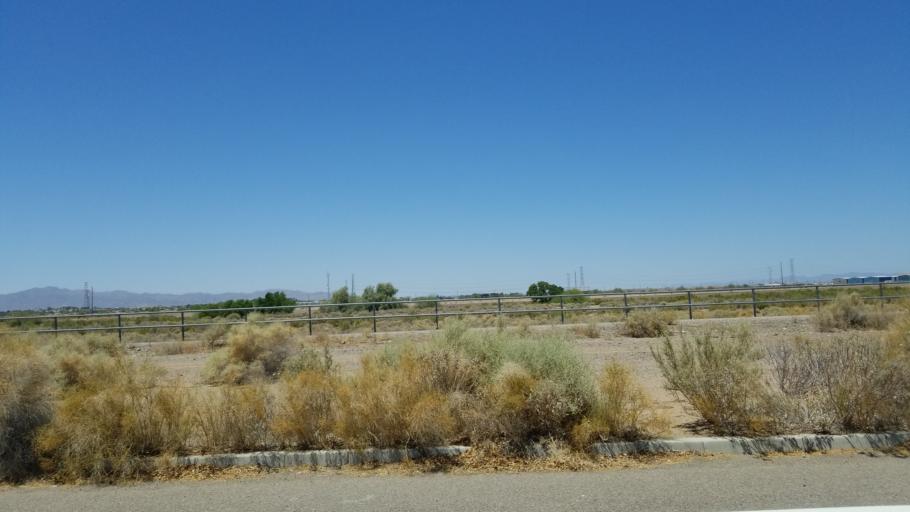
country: US
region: Arizona
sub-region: Maricopa County
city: Litchfield Park
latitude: 33.5155
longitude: -112.2974
